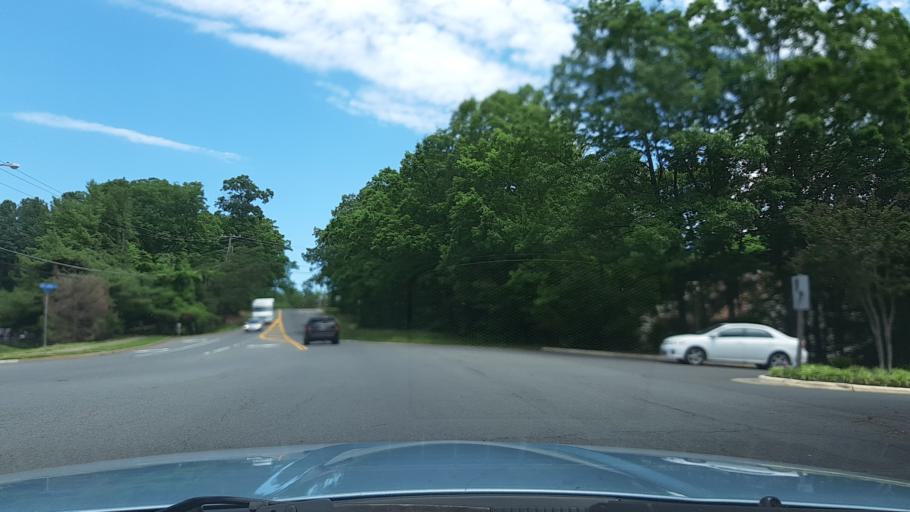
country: US
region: Virginia
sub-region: Fairfax County
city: Newington
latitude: 38.7278
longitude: -77.2097
